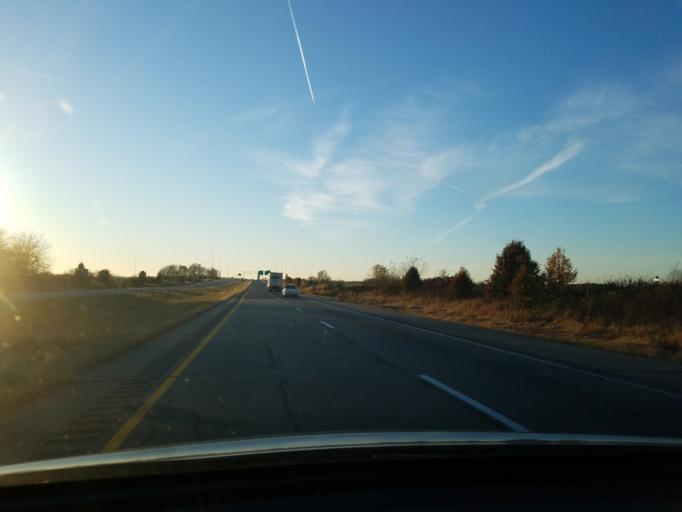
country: US
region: Indiana
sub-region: Gibson County
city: Haubstadt
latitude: 38.1670
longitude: -87.5397
